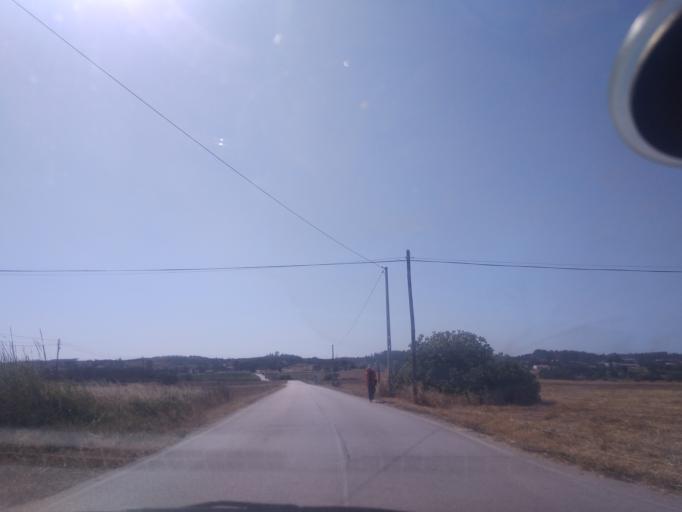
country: PT
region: Faro
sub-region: Aljezur
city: Aljezur
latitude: 37.2279
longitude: -8.8239
